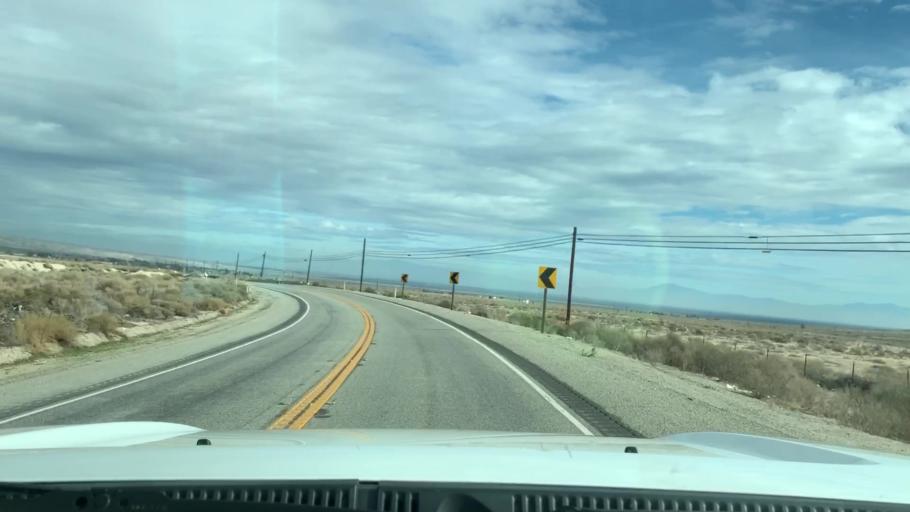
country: US
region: California
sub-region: Kern County
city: Ford City
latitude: 35.1882
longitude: -119.4375
